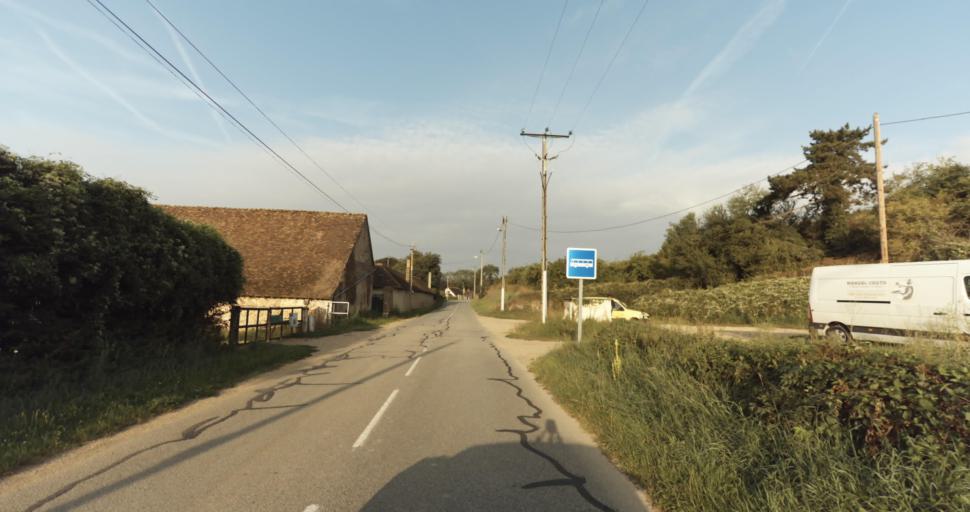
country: FR
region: Centre
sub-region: Departement d'Eure-et-Loir
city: Vert-en-Drouais
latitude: 48.7646
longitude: 1.3207
